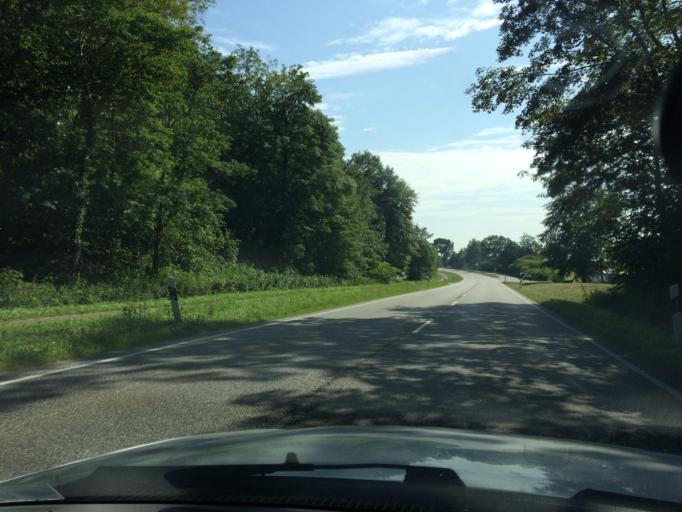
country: DE
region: Schleswig-Holstein
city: Oeversee
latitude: 54.7151
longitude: 9.4424
